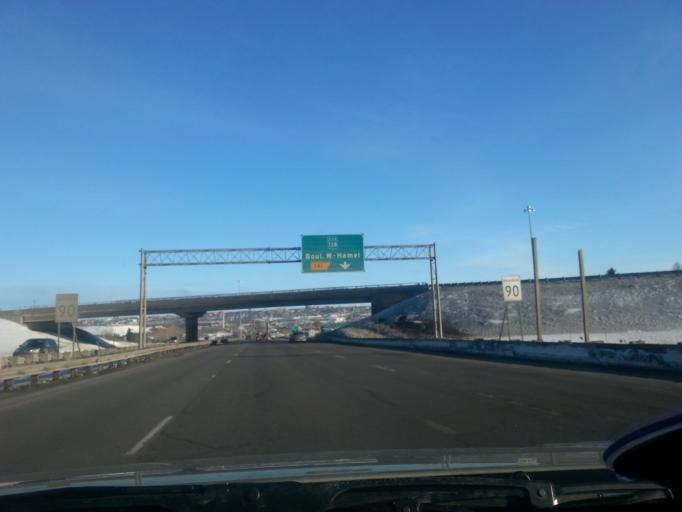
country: CA
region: Quebec
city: L'Ancienne-Lorette
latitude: 46.8105
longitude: -71.3377
